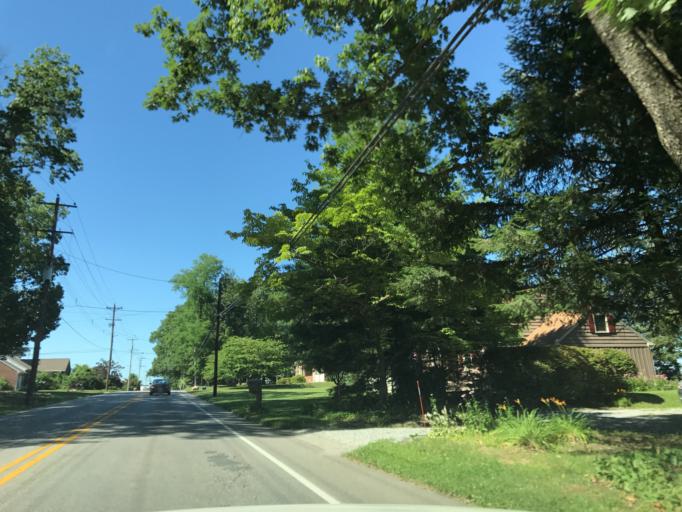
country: US
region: Pennsylvania
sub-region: York County
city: Parkville
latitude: 39.7904
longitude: -76.9444
